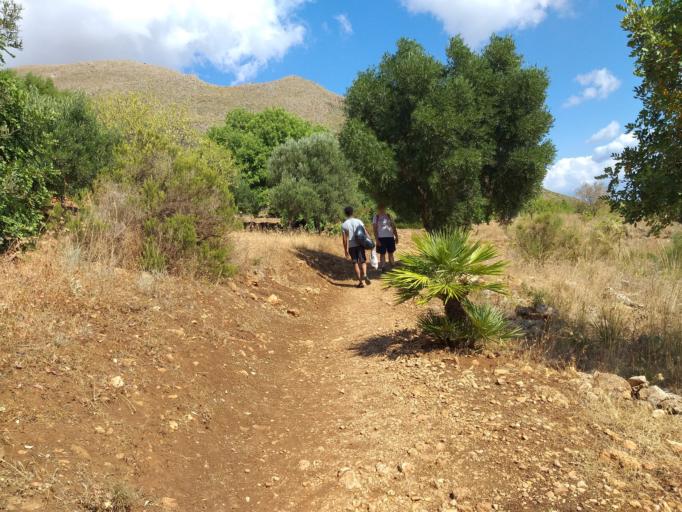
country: IT
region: Sicily
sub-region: Trapani
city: Castelluzzo
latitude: 38.0853
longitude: 12.8065
